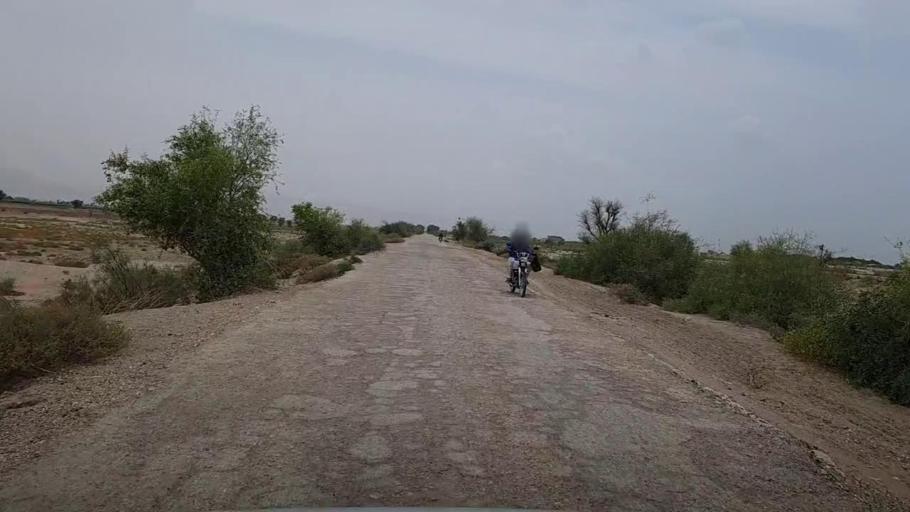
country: PK
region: Sindh
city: Sann
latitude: 26.2001
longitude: 67.9737
